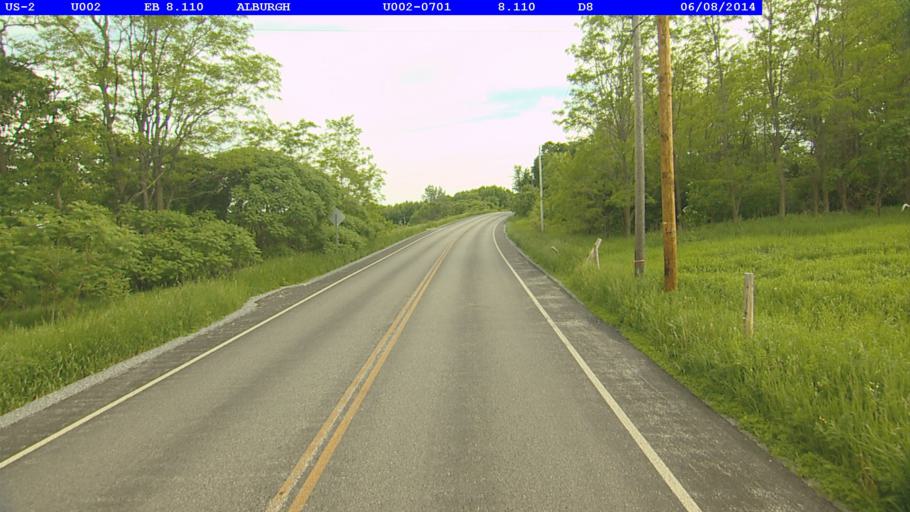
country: US
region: New York
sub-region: Clinton County
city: Rouses Point
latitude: 44.9339
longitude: -73.2734
